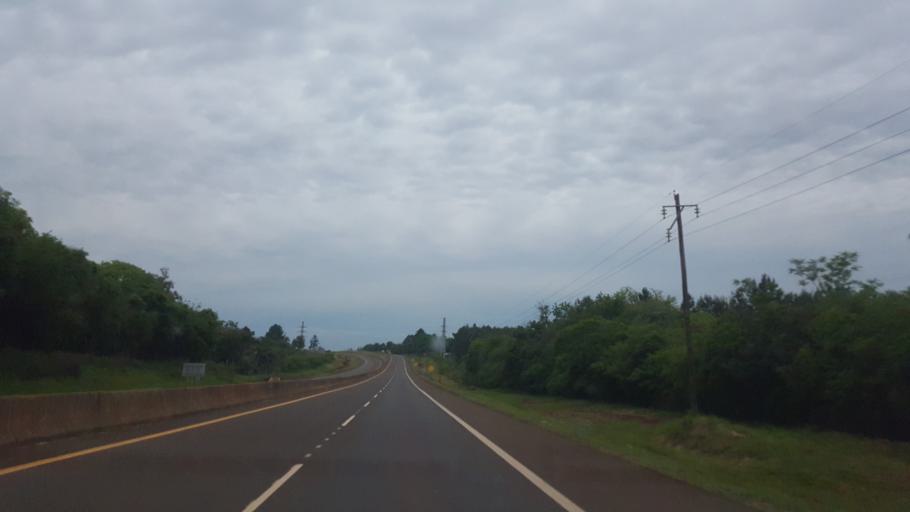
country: AR
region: Misiones
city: Garupa
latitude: -27.5436
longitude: -55.8526
